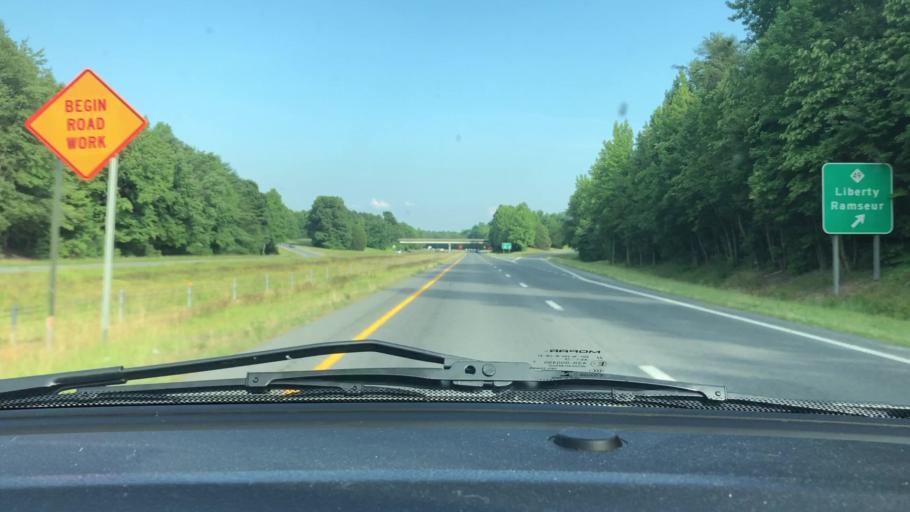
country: US
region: North Carolina
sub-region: Randolph County
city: Liberty
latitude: 35.8261
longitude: -79.5777
